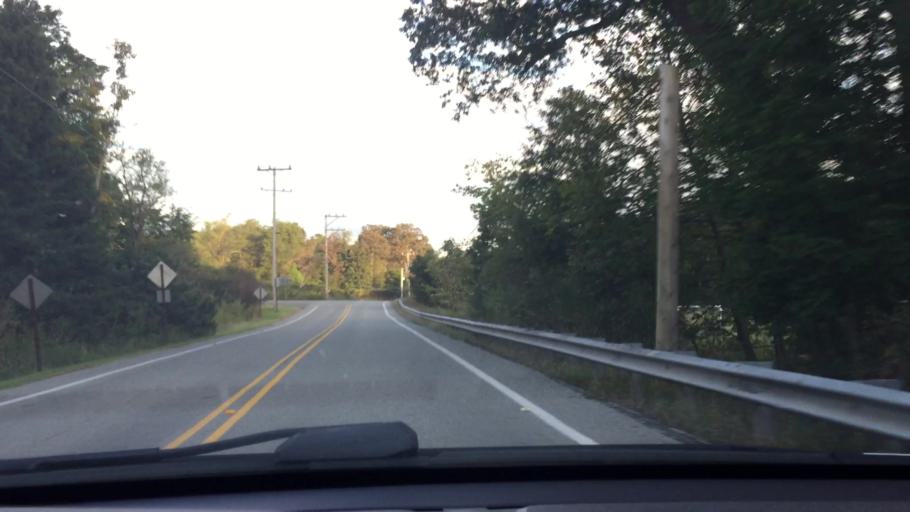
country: US
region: Pennsylvania
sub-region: Westmoreland County
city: Murrysville
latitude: 40.4548
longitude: -79.7344
